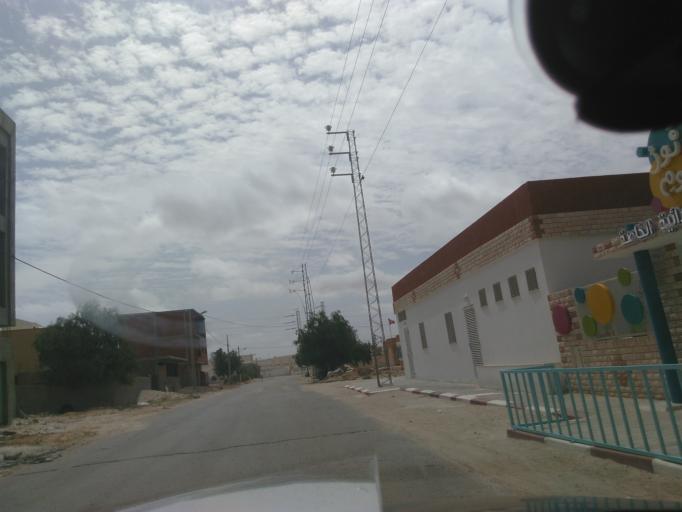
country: TN
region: Tataouine
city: Tataouine
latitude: 32.9516
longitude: 10.4705
